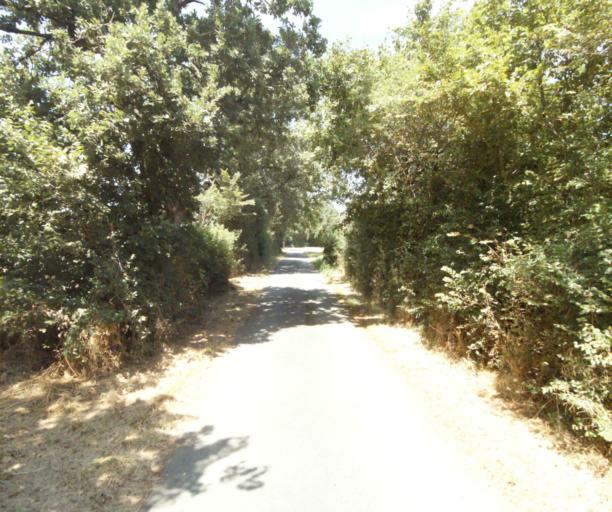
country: FR
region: Midi-Pyrenees
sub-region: Departement du Tarn
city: Soreze
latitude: 43.4930
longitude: 2.0568
